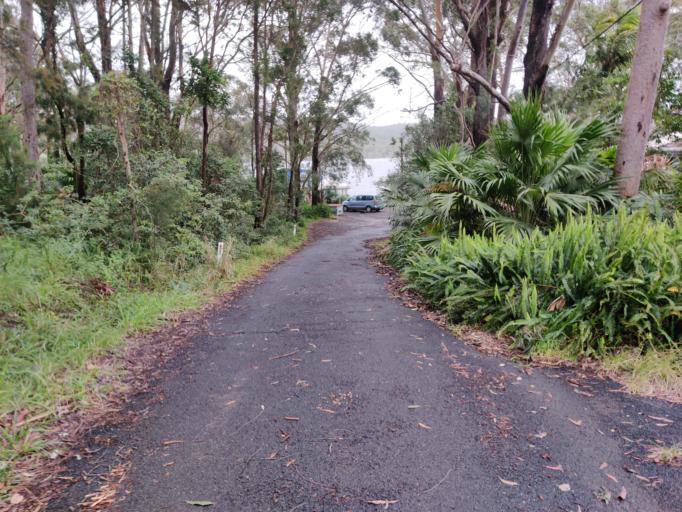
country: AU
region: New South Wales
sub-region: Great Lakes
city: Forster
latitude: -32.3896
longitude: 152.5024
